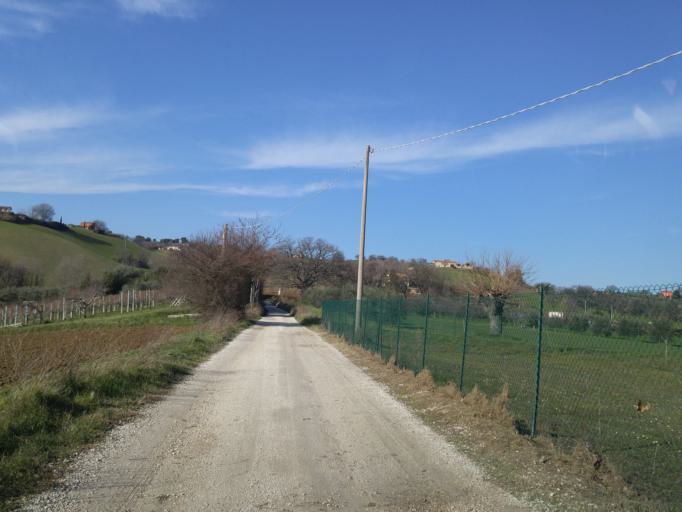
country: IT
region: The Marches
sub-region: Provincia di Pesaro e Urbino
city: Calcinelli
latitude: 43.7581
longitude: 12.9137
